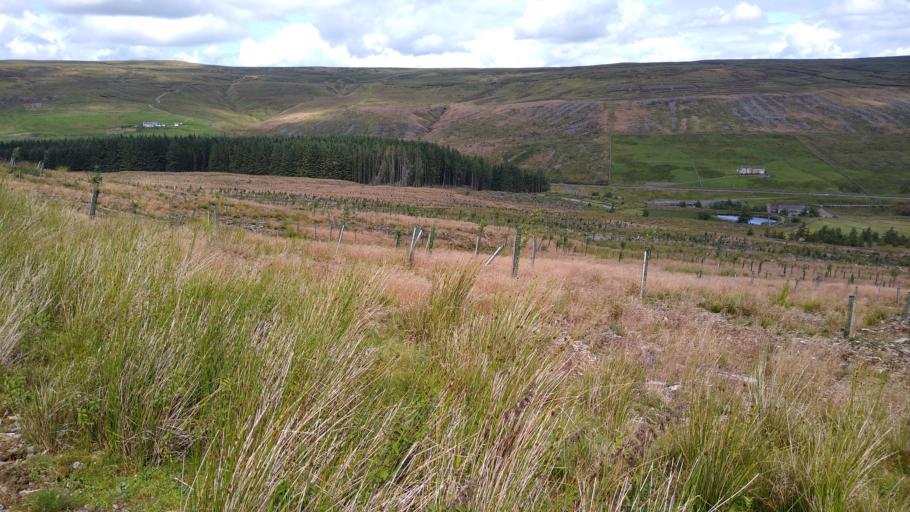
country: GB
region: England
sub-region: County Durham
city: Holwick
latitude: 54.7774
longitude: -2.2765
